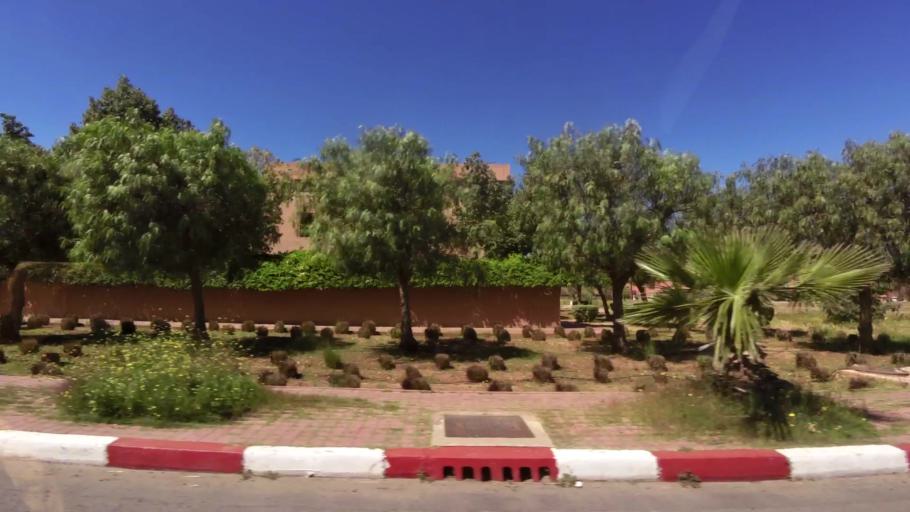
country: MA
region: Marrakech-Tensift-Al Haouz
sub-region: Marrakech
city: Marrakesh
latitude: 31.5900
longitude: -7.9850
